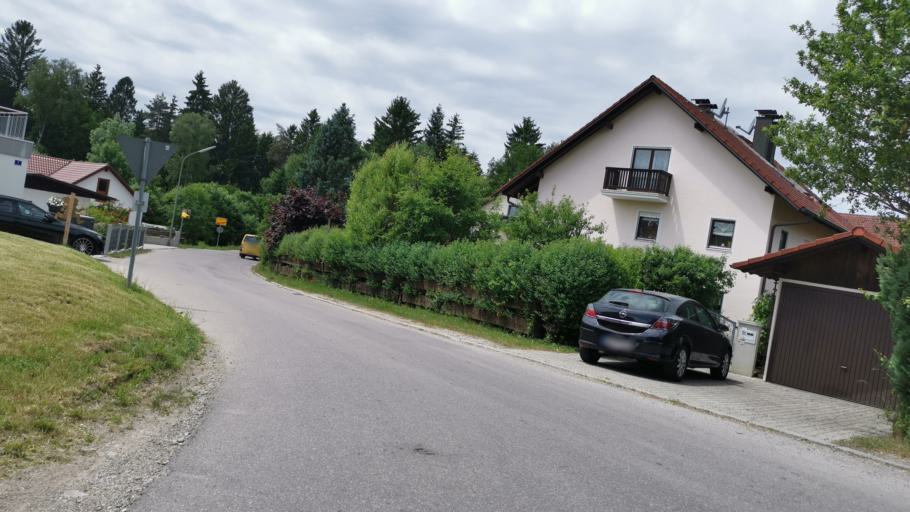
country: DE
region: Bavaria
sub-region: Upper Bavaria
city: Hattenhofen
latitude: 48.2223
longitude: 11.0973
